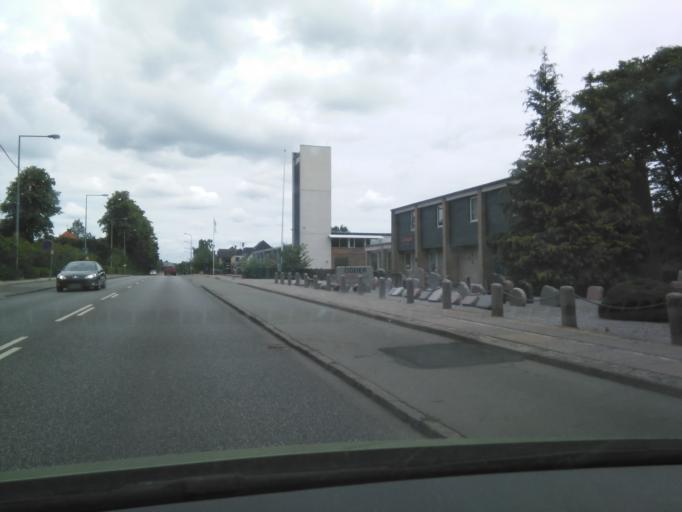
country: DK
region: Central Jutland
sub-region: Odder Kommune
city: Odder
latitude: 55.9757
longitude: 10.1504
